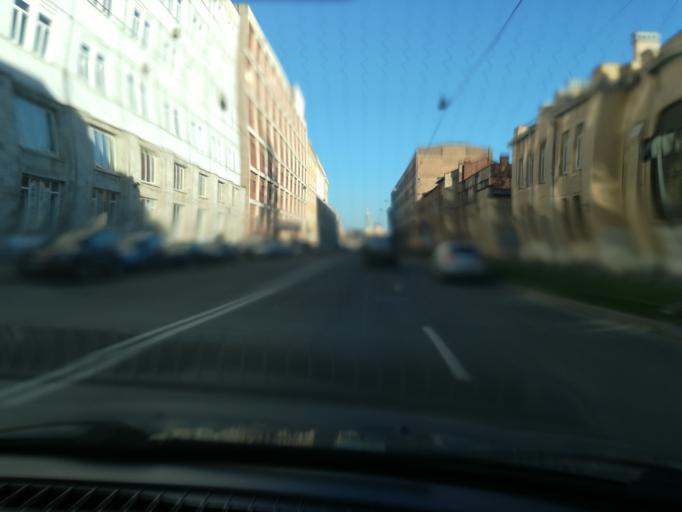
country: RU
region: St.-Petersburg
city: Vasyl'evsky Ostrov
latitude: 59.9313
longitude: 30.2648
